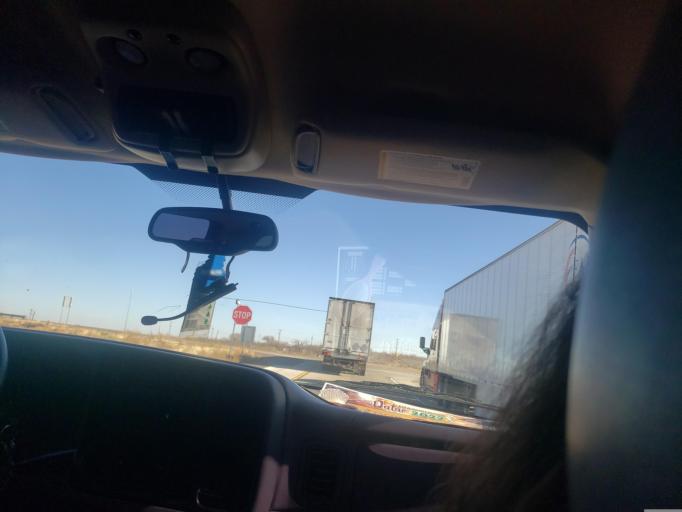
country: US
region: New Mexico
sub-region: Quay County
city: Tucumcari
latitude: 35.1548
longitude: -103.7028
